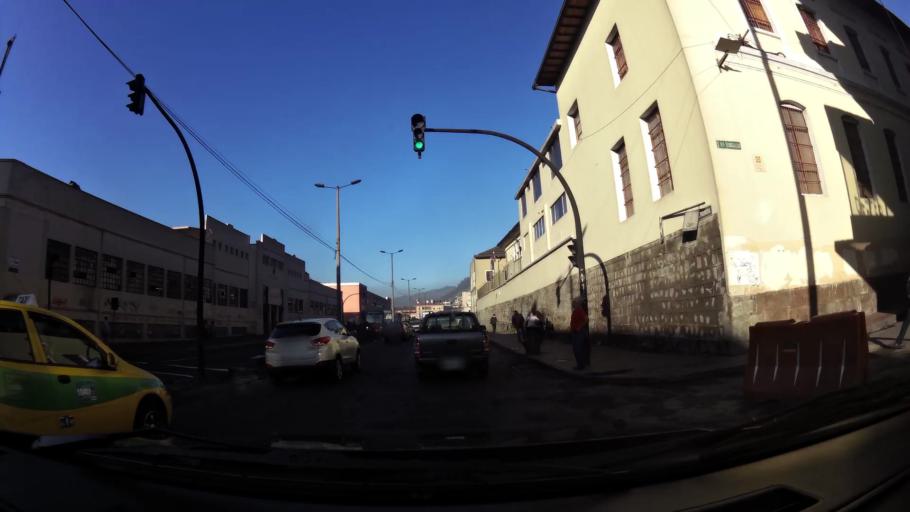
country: EC
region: Pichincha
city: Quito
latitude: -0.2194
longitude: -78.5071
